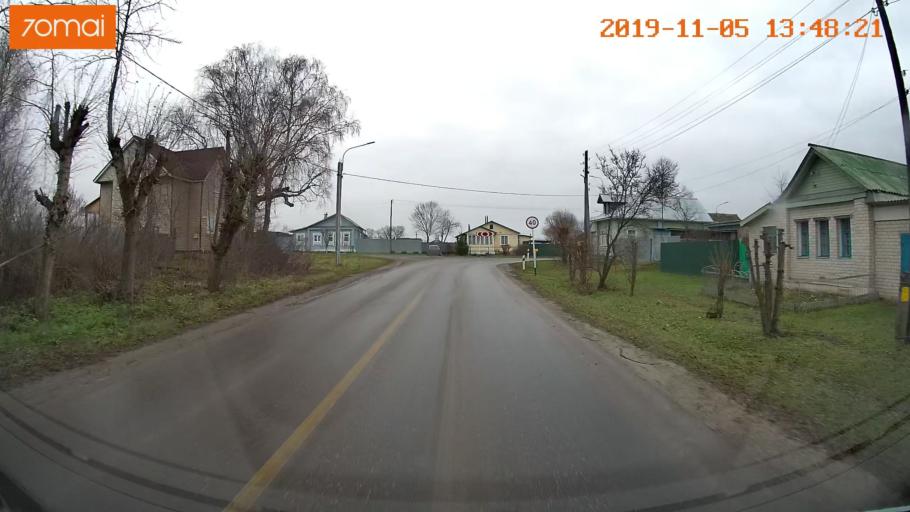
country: RU
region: Ivanovo
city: Shuya
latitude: 57.0036
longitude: 41.4057
